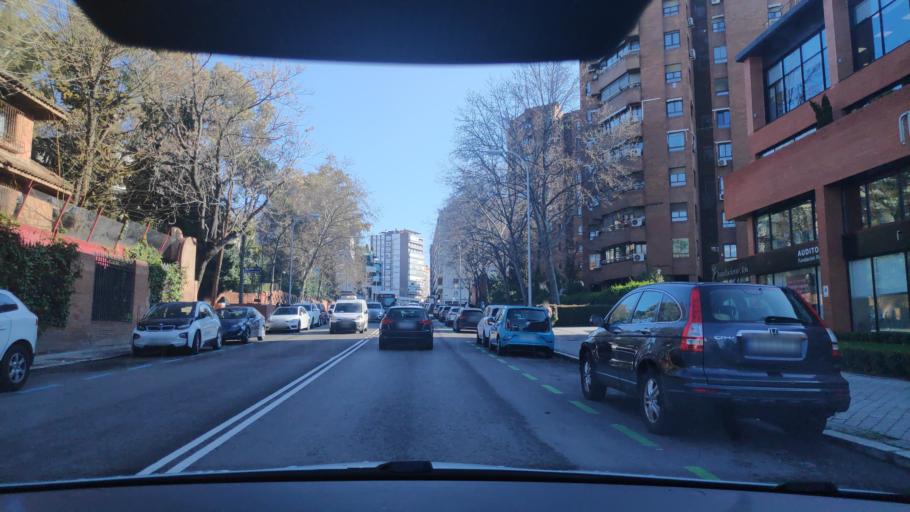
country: ES
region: Madrid
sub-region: Provincia de Madrid
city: Chamartin
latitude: 40.4545
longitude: -3.6834
